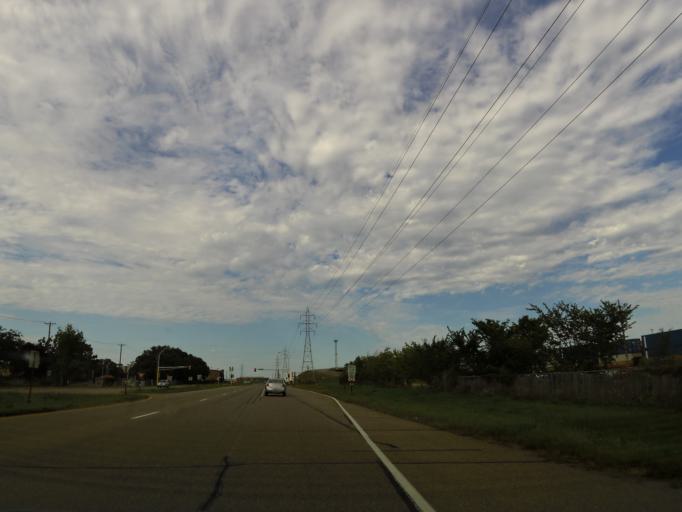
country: US
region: Minnesota
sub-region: Anoka County
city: Columbia Heights
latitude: 45.0412
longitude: -93.2752
